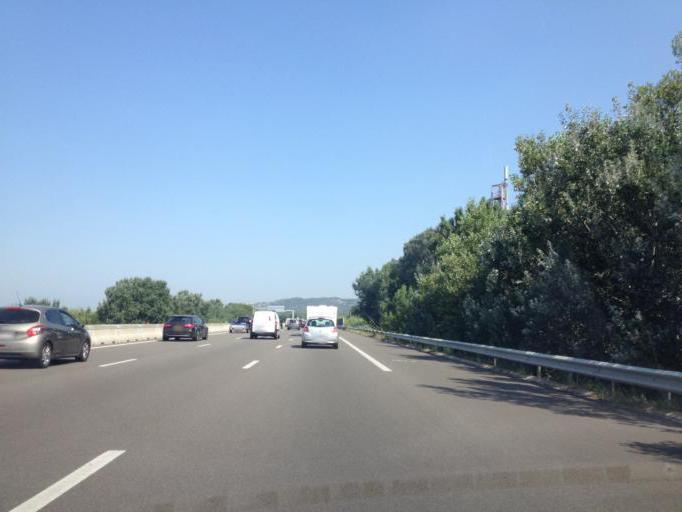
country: FR
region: Provence-Alpes-Cote d'Azur
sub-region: Departement du Vaucluse
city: Piolenc
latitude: 44.1768
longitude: 4.7566
